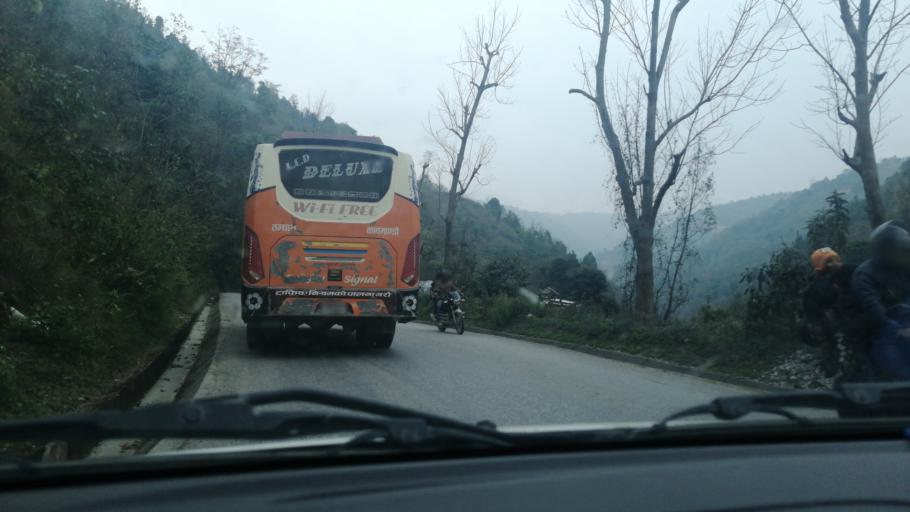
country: NP
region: Western Region
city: Tansen
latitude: 27.8146
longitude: 83.5313
